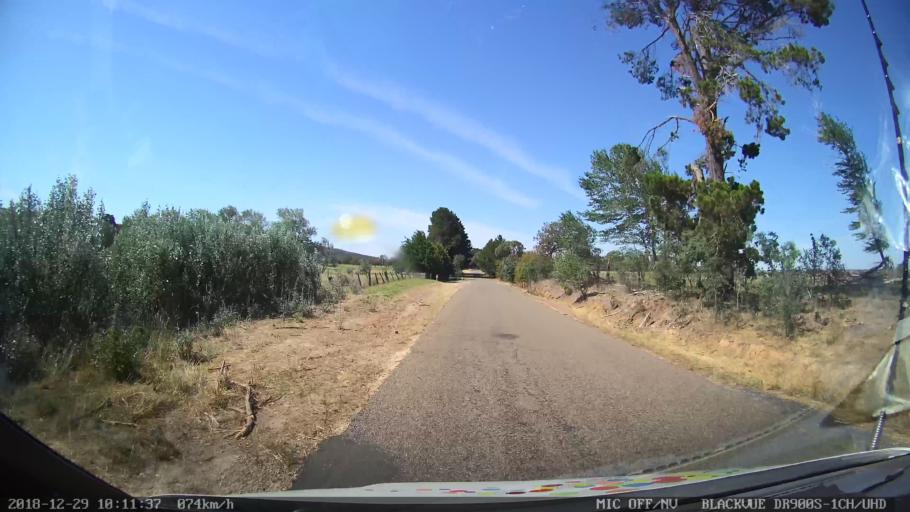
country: AU
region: New South Wales
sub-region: Yass Valley
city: Gundaroo
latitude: -34.8856
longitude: 149.4515
